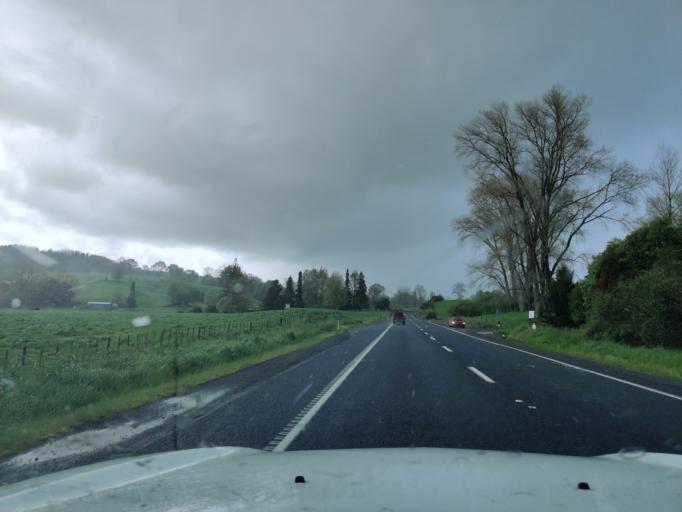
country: NZ
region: Waikato
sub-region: Matamata-Piako District
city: Matamata
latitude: -37.9773
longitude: 175.6985
